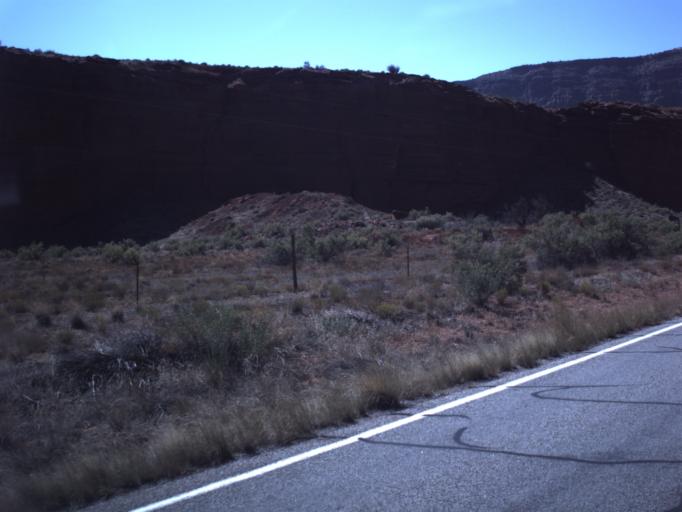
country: US
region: Utah
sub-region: Grand County
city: Moab
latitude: 38.6819
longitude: -109.4309
